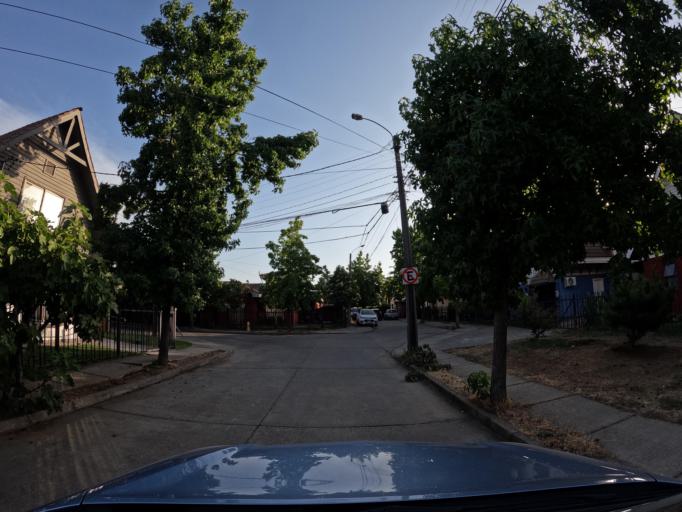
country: CL
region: Maule
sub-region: Provincia de Talca
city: Talca
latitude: -35.4336
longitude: -71.6222
